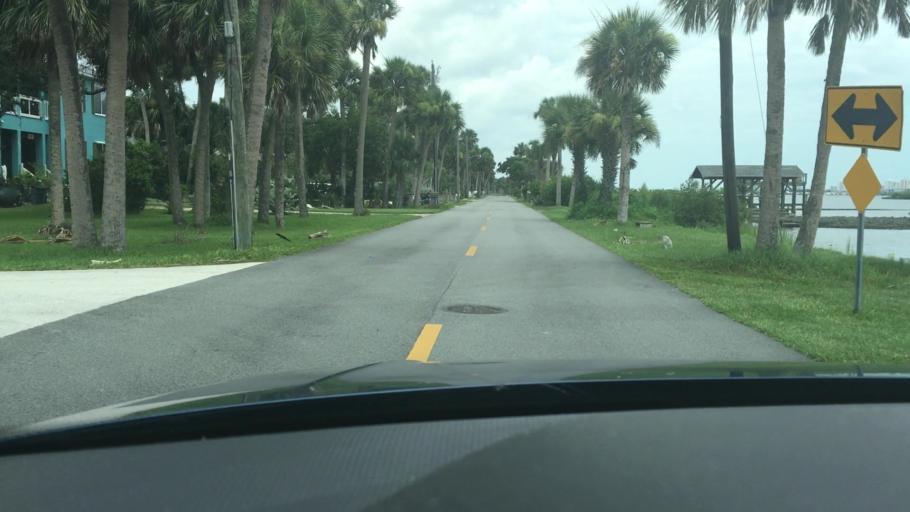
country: US
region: Florida
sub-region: Volusia County
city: Port Orange
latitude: 29.1268
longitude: -80.9772
